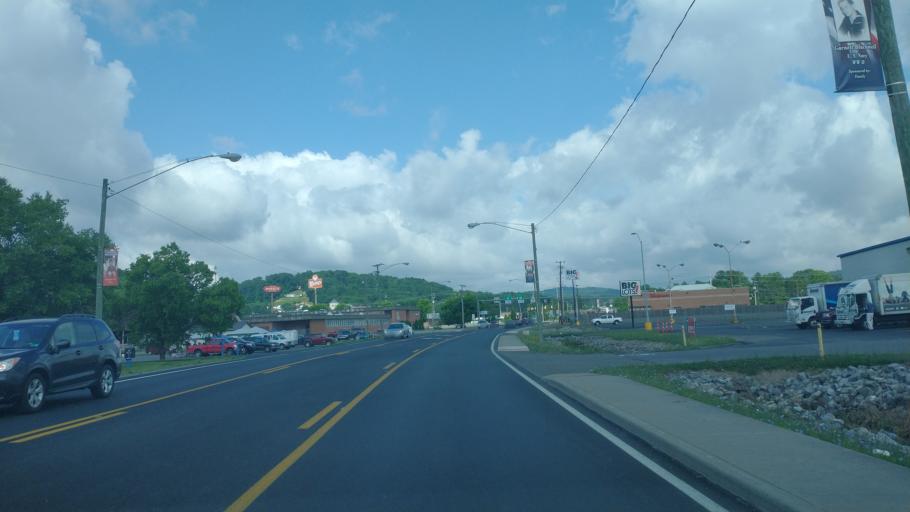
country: US
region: West Virginia
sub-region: Mercer County
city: Princeton
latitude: 37.3603
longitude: -81.1020
